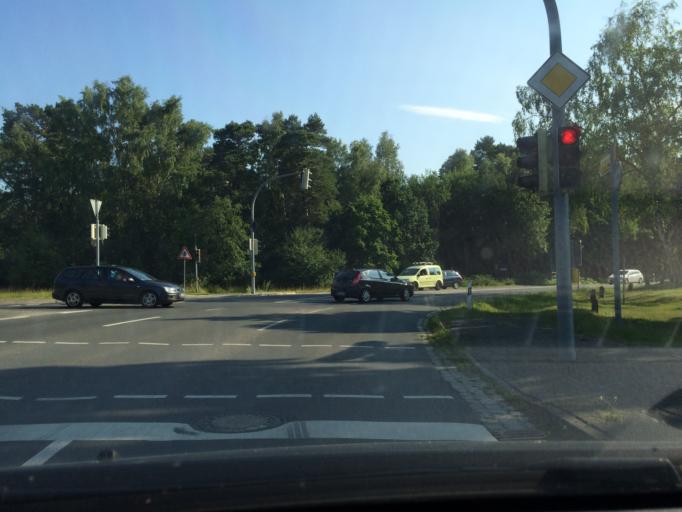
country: DE
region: Mecklenburg-Vorpommern
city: Ostseebad Binz
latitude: 54.4401
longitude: 13.5665
